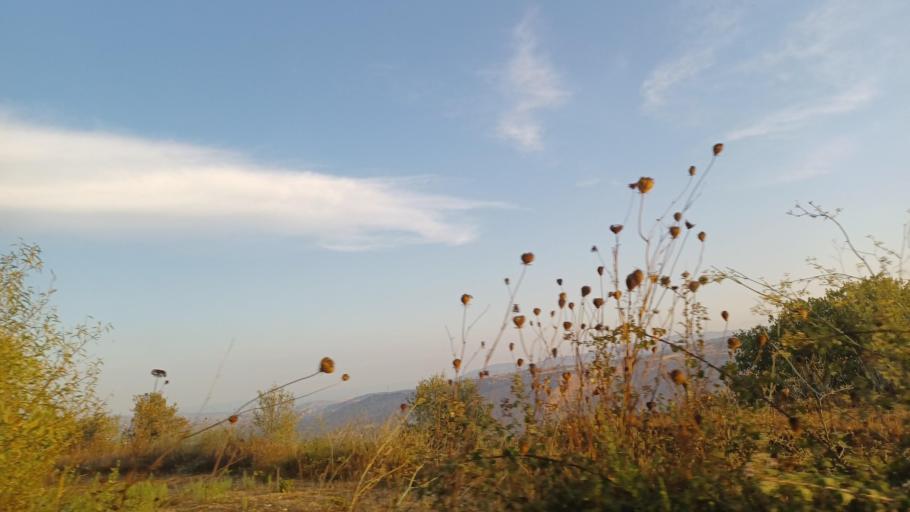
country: CY
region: Pafos
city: Tala
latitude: 34.8978
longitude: 32.5010
